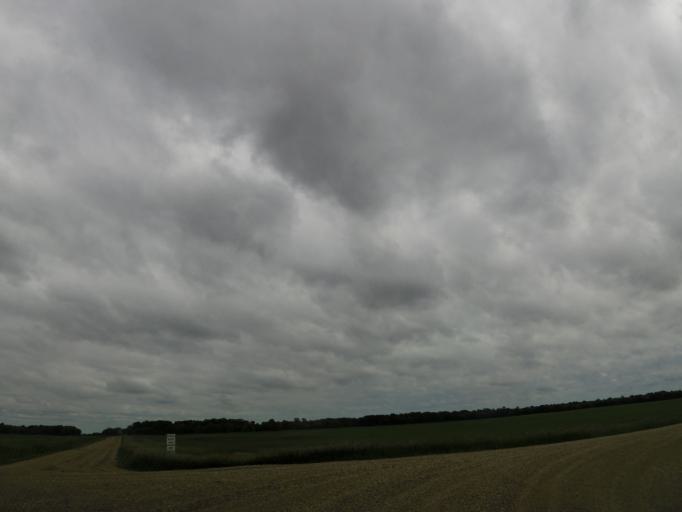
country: US
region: North Dakota
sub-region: Walsh County
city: Grafton
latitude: 48.4559
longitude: -97.4919
